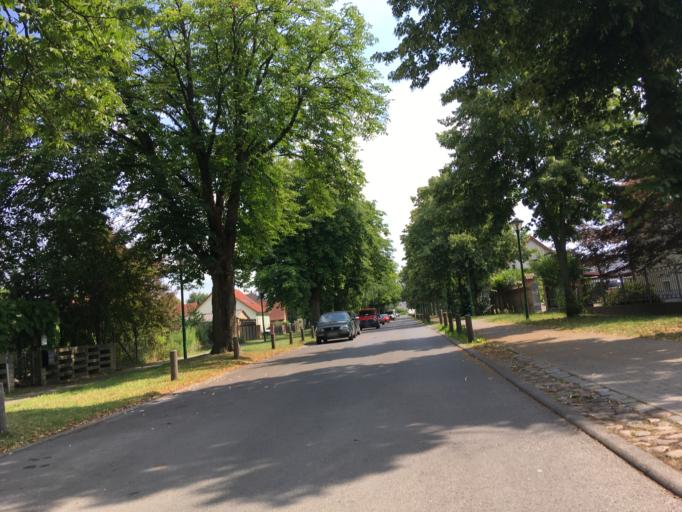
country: DE
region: Brandenburg
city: Glienicke
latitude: 52.6592
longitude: 13.3370
